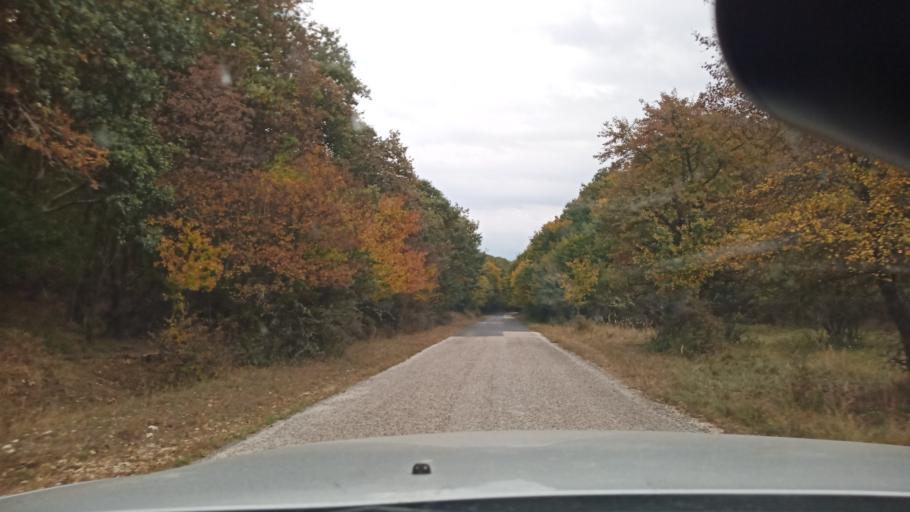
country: HU
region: Fejer
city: Zamoly
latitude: 47.3723
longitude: 18.3396
